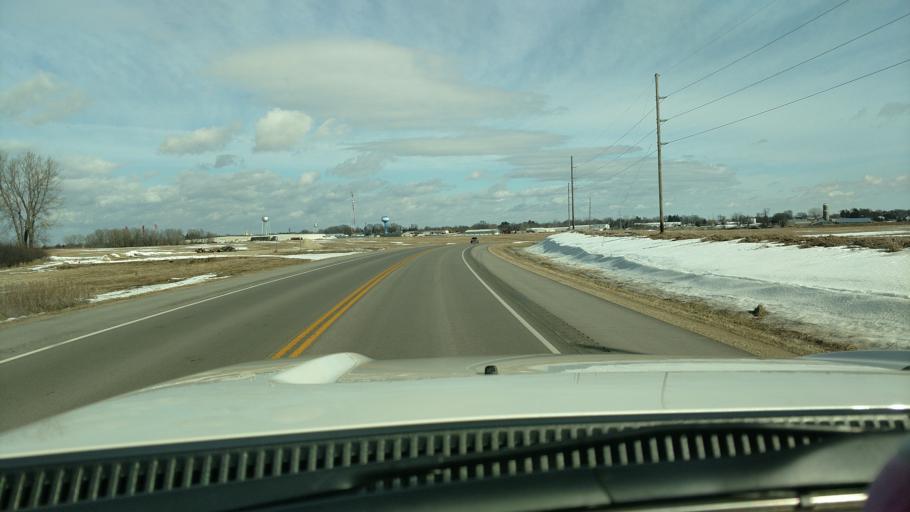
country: US
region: Minnesota
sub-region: Wabasha County
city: Plainview
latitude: 44.1572
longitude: -92.1926
